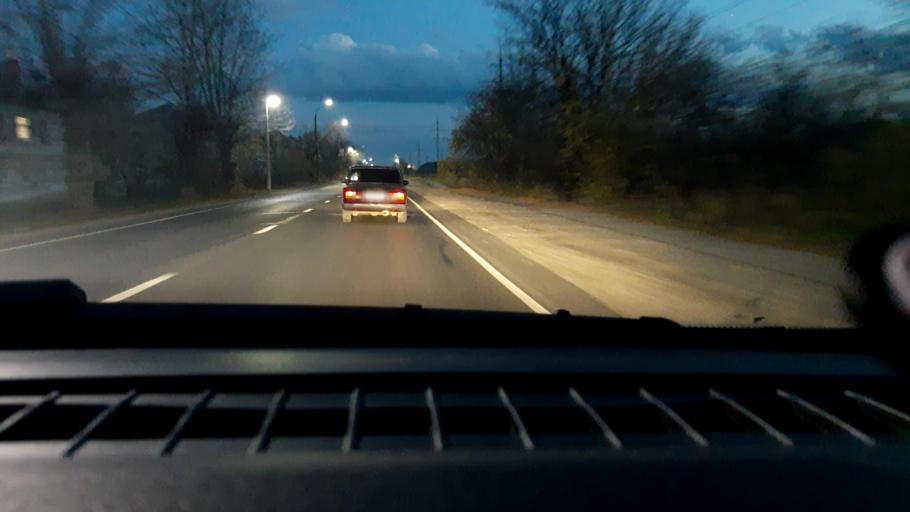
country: RU
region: Nizjnij Novgorod
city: Novaya Balakhna
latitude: 56.4825
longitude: 43.6013
